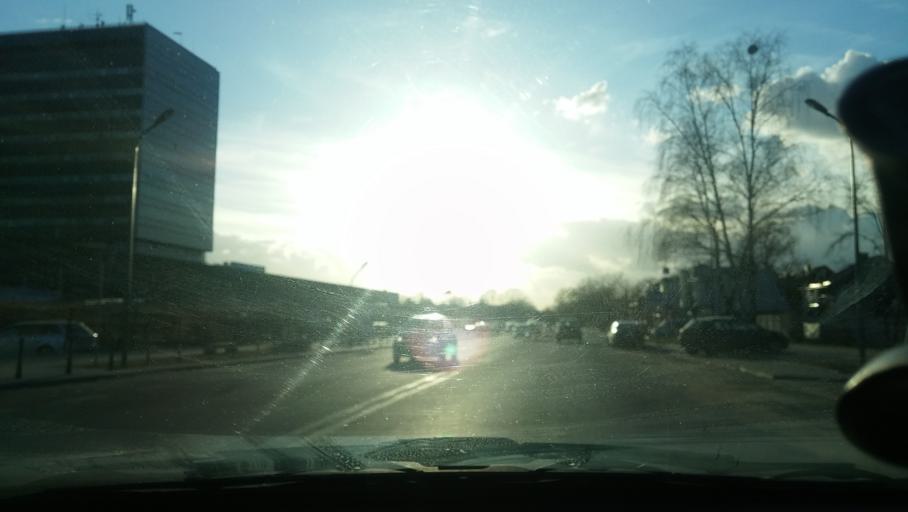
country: PL
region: Masovian Voivodeship
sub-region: Warszawa
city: Wawer
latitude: 52.2075
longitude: 21.1938
